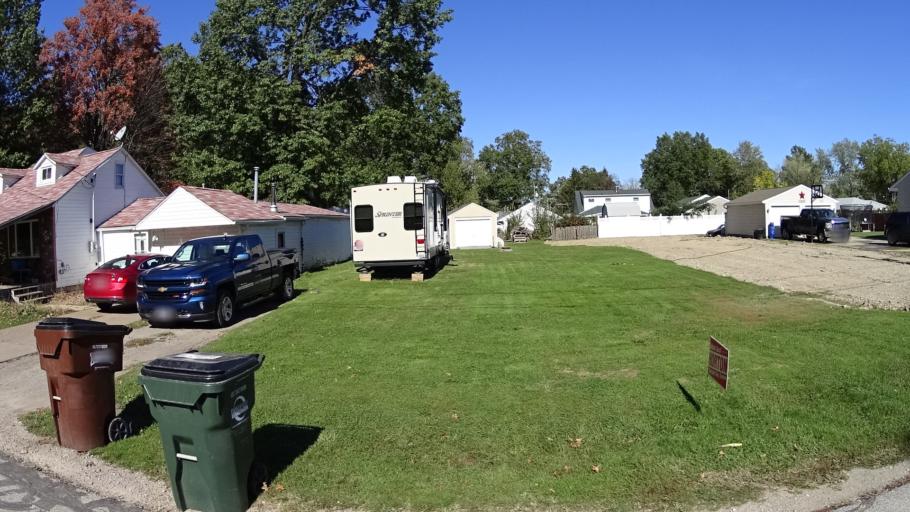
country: US
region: Ohio
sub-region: Lorain County
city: Lorain
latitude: 41.4251
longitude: -82.1598
